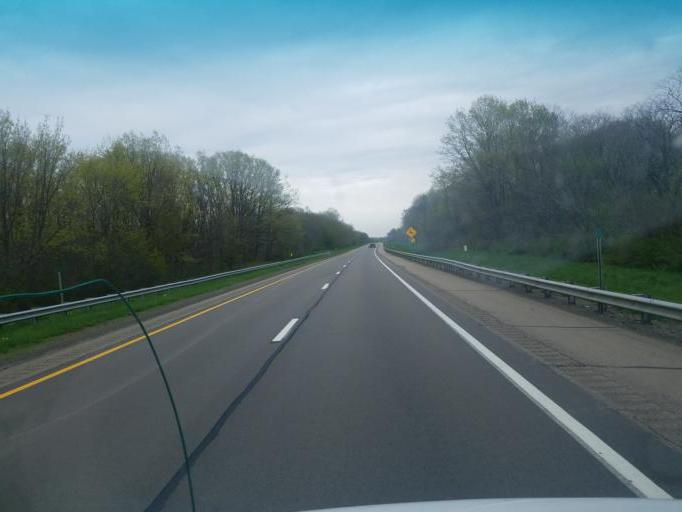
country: US
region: New York
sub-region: Chautauqua County
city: Westfield
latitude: 42.3671
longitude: -79.5178
